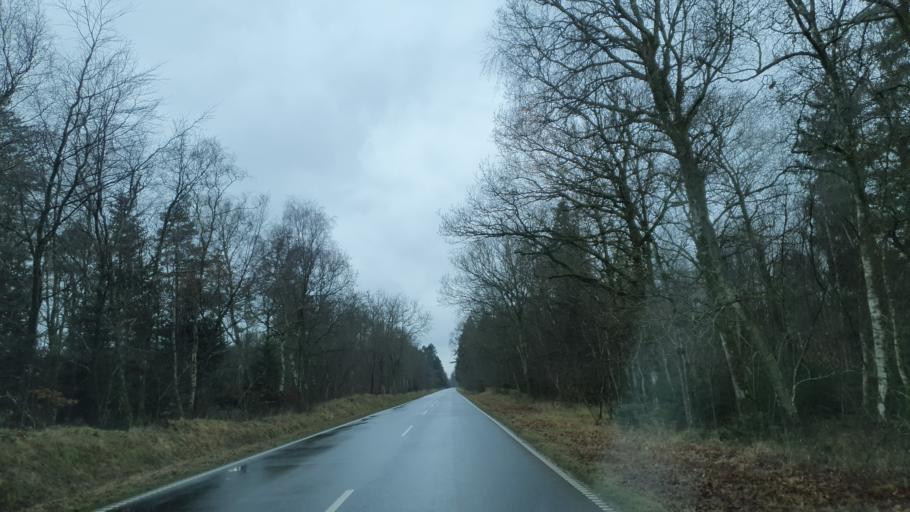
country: DK
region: North Denmark
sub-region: Jammerbugt Kommune
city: Fjerritslev
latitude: 57.1268
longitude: 9.1311
